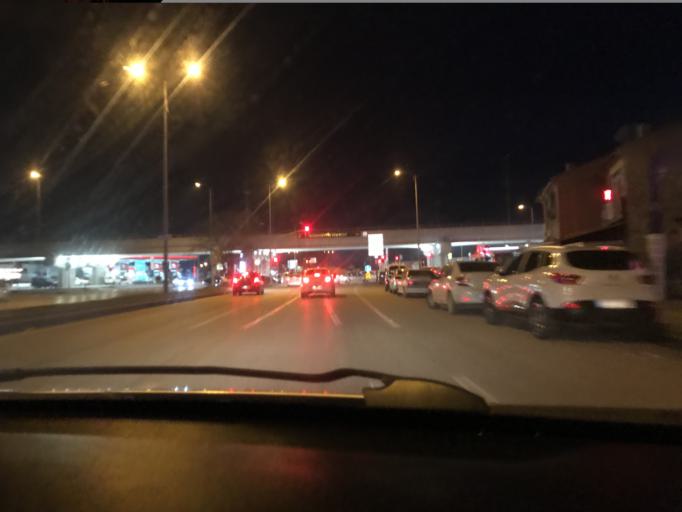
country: TR
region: Ankara
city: Batikent
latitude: 39.9490
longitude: 32.7383
